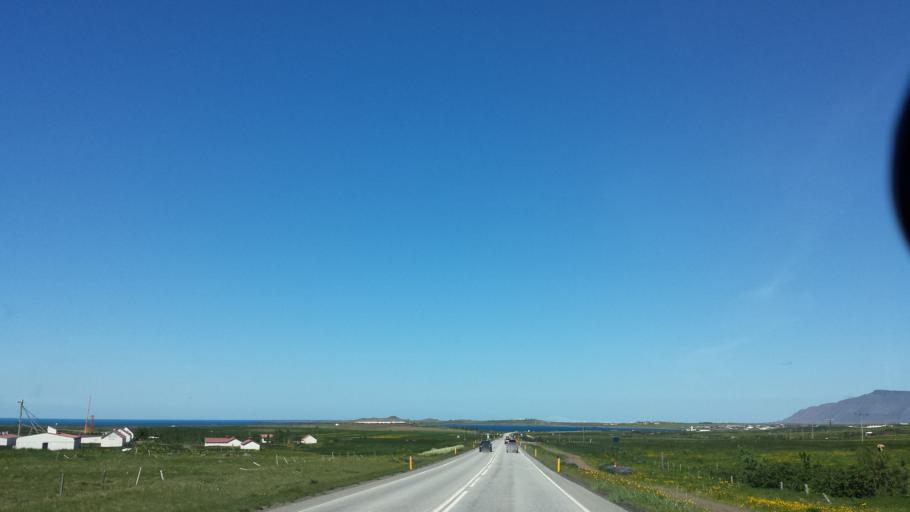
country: IS
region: Capital Region
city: Mosfellsbaer
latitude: 64.2133
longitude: -21.7755
